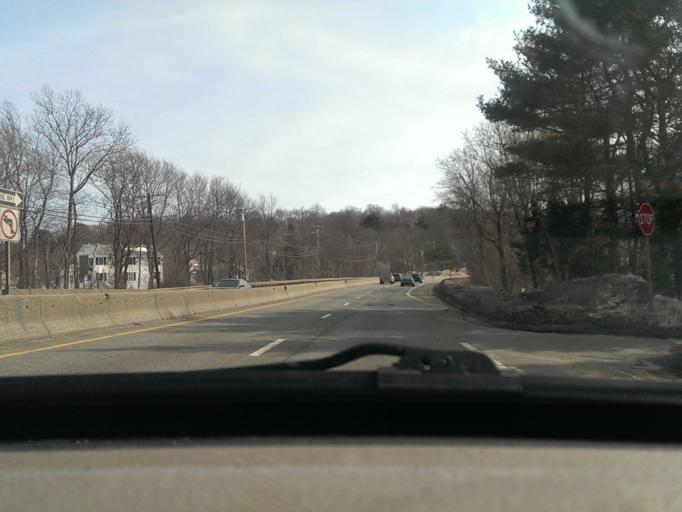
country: US
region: Massachusetts
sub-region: Worcester County
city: Millbury
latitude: 42.1866
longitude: -71.7653
